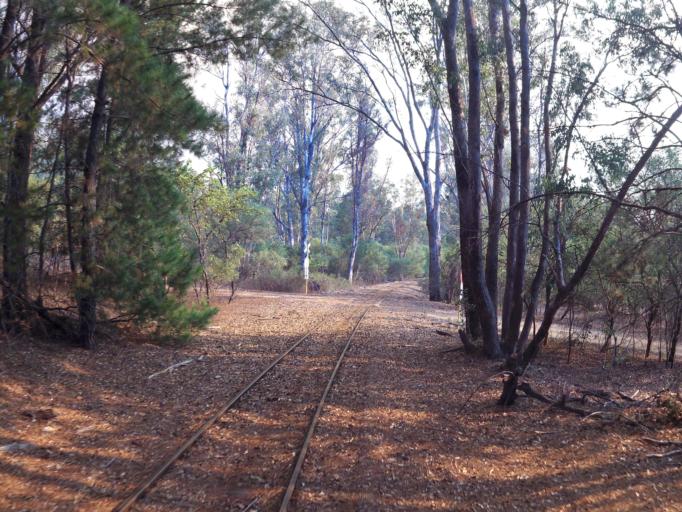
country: AU
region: Western Australia
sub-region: Waroona
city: Waroona
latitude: -32.7383
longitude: 116.1303
